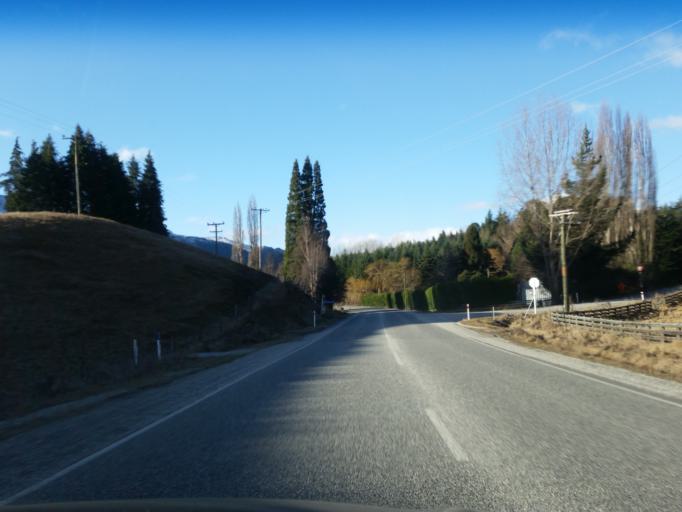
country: NZ
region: Otago
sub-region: Queenstown-Lakes District
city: Queenstown
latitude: -44.9614
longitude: 168.7219
